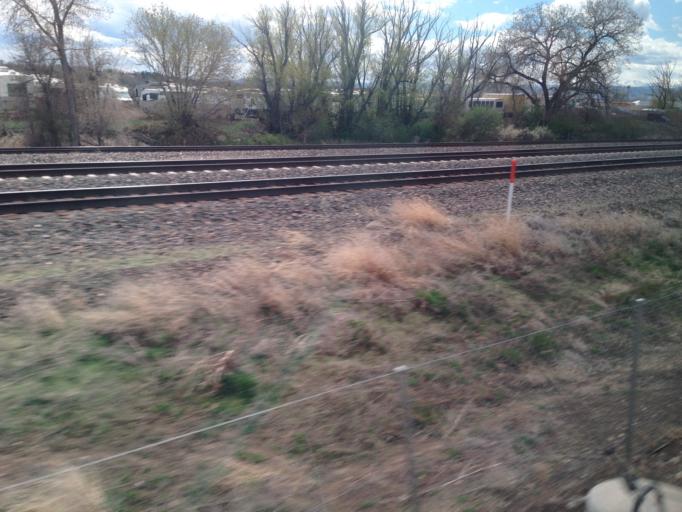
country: US
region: Colorado
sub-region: Adams County
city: Berkley
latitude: 39.8046
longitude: -105.0362
